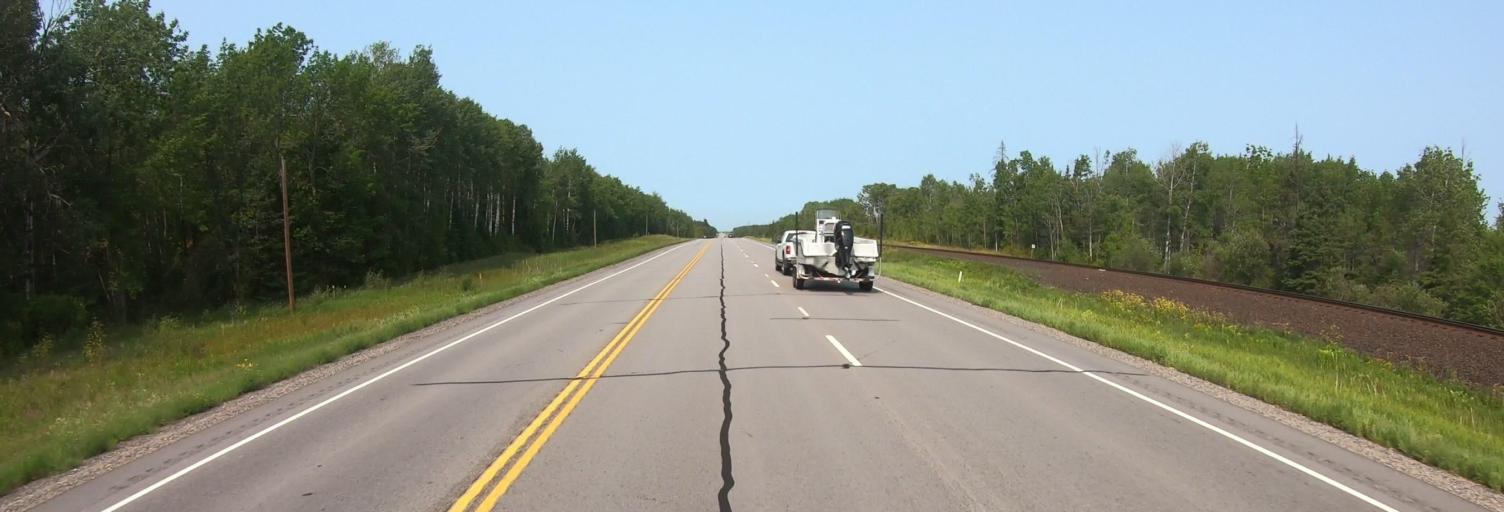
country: CA
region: Ontario
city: Fort Frances
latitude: 48.4490
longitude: -93.2666
